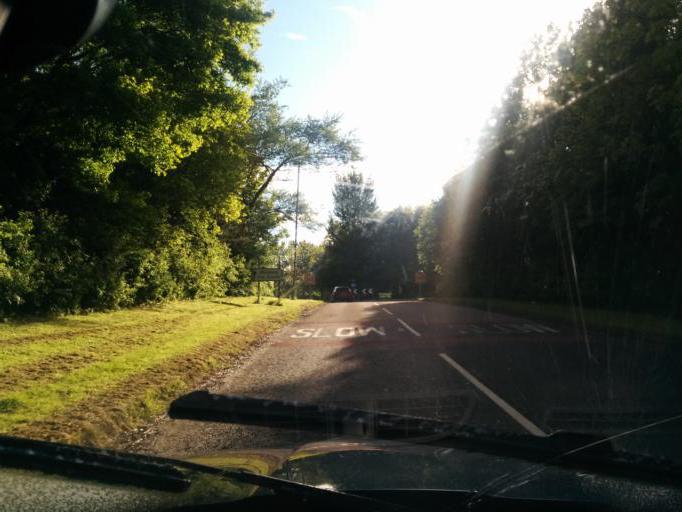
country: GB
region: England
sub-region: Northumberland
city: Cramlington
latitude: 55.0877
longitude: -1.6118
